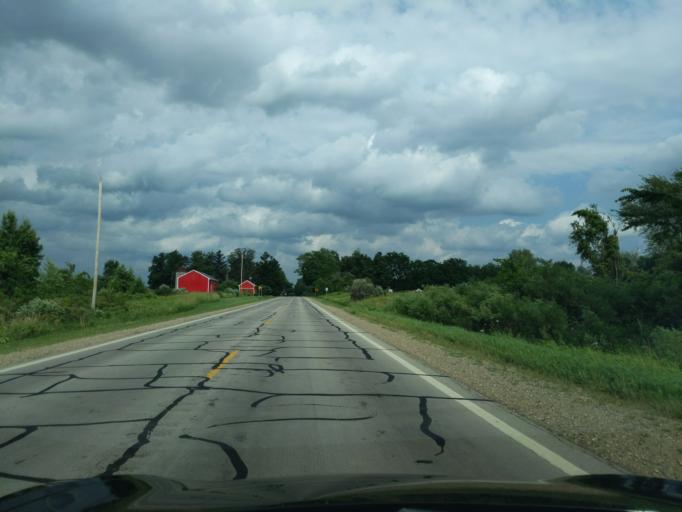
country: US
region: Michigan
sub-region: Eaton County
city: Eaton Rapids
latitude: 42.4149
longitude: -84.6160
